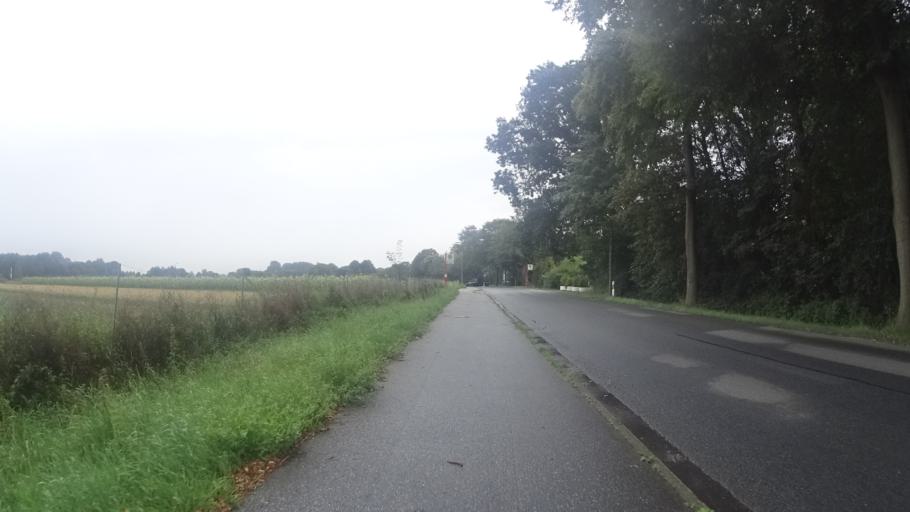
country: DE
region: Schleswig-Holstein
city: Seeth-Ekholt
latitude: 53.7561
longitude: 9.7173
